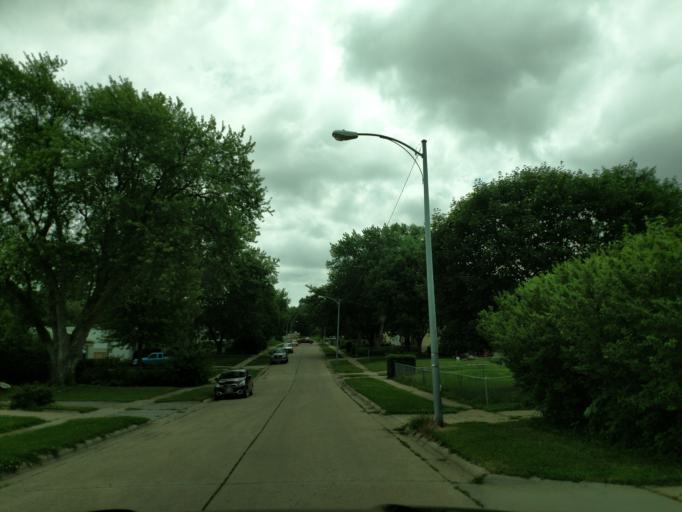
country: US
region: Nebraska
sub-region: Sarpy County
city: La Vista
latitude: 41.2093
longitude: -96.0000
